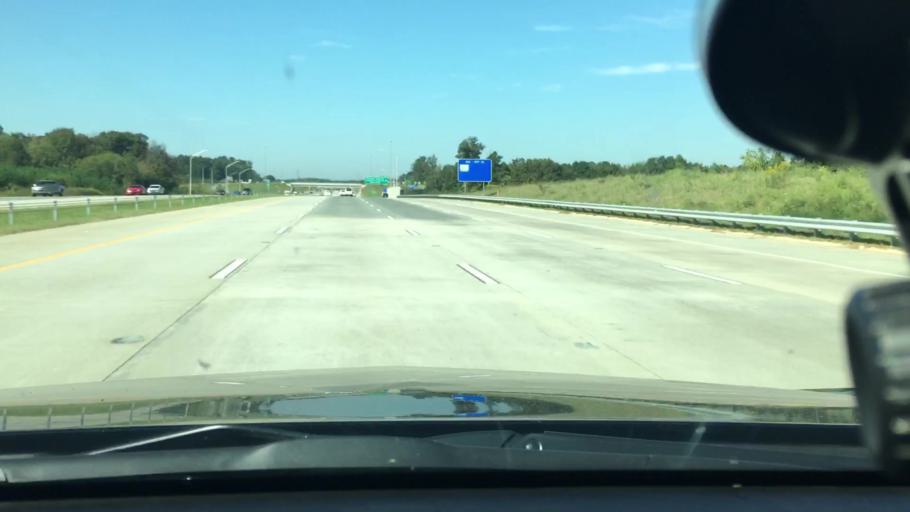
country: US
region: North Carolina
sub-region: Mecklenburg County
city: Huntersville
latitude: 35.3685
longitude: -80.7723
